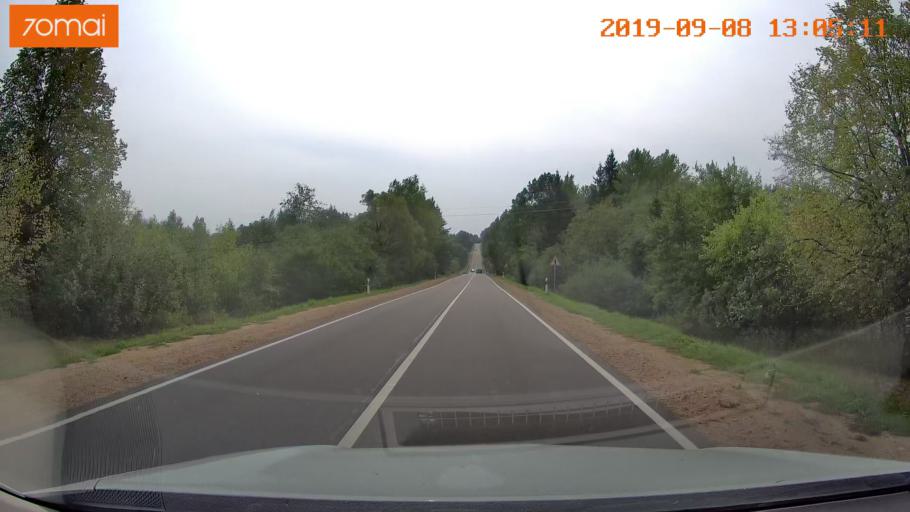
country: LT
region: Kauno apskritis
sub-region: Kauno rajonas
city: Karmelava
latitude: 54.8568
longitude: 24.2361
